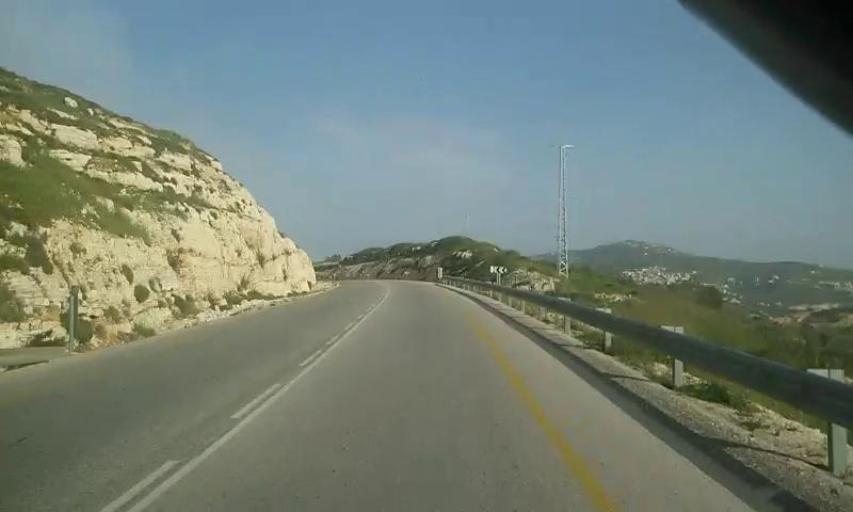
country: PS
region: West Bank
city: Sarrah
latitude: 32.1913
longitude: 35.1959
